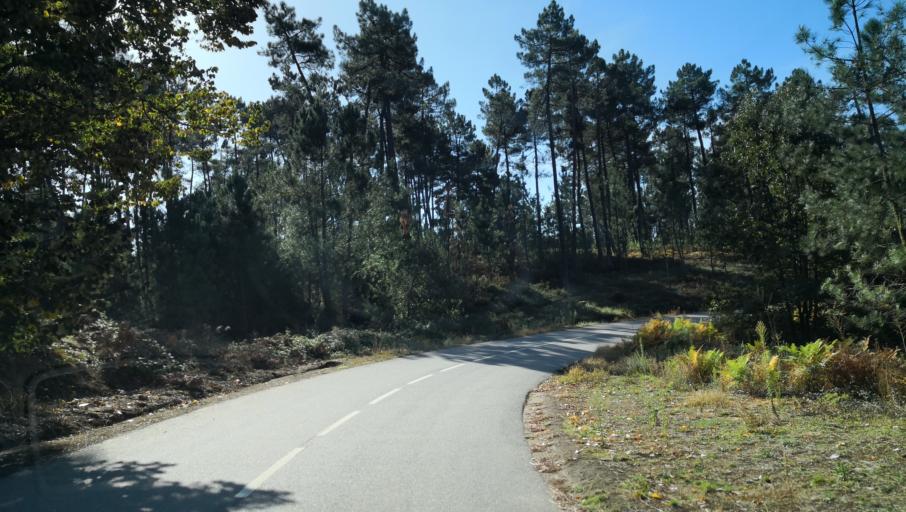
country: PT
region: Vila Real
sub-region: Sabrosa
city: Vilela
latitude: 41.2439
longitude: -7.6353
